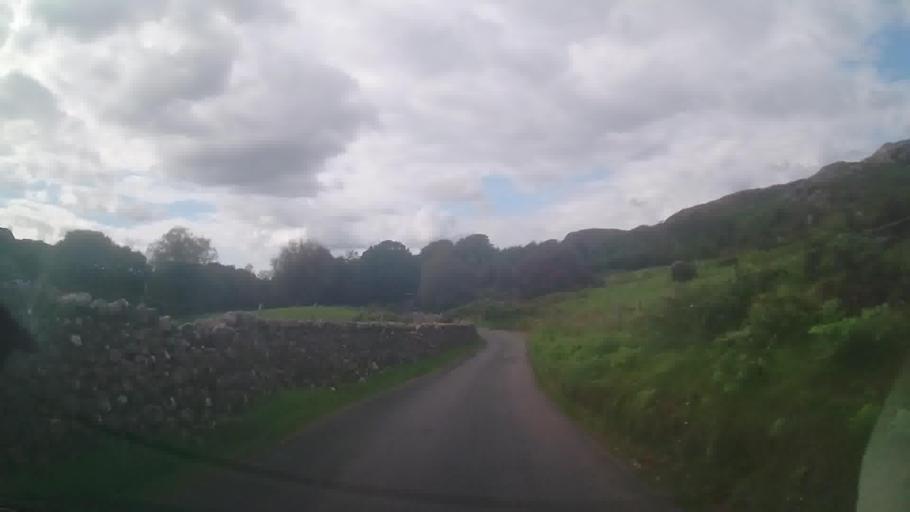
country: GB
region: England
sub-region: Cumbria
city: Millom
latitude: 54.3973
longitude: -3.2376
